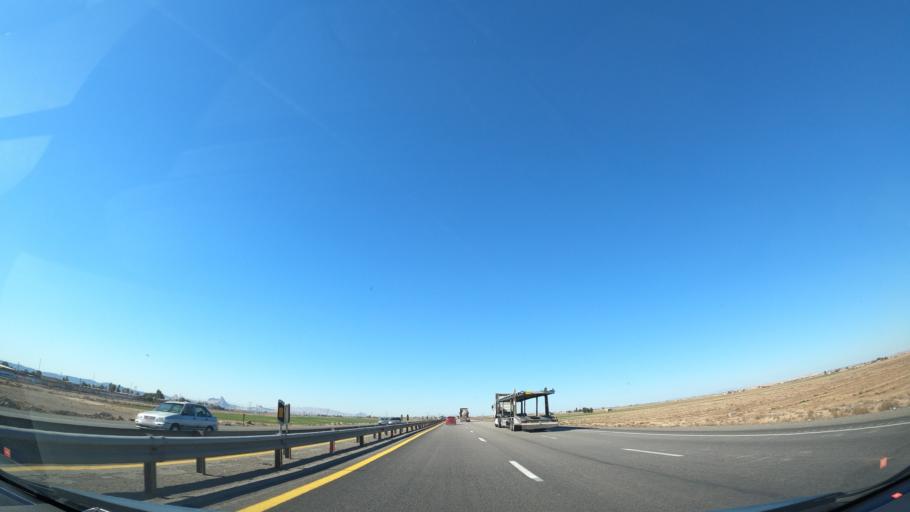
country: IR
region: Qom
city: Qom
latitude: 34.5580
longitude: 51.0000
